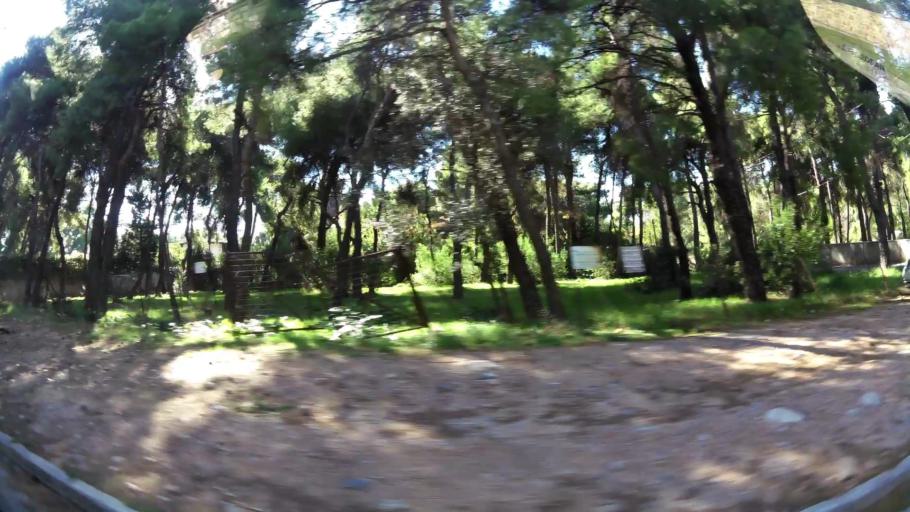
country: GR
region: Attica
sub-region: Nomarchia Athinas
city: Ekali
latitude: 38.1143
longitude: 23.8381
